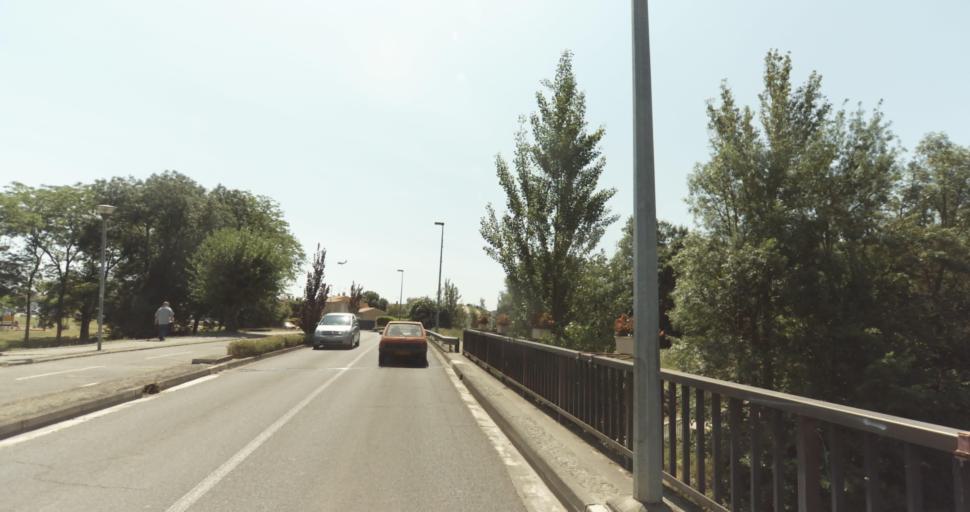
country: FR
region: Midi-Pyrenees
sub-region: Departement de la Haute-Garonne
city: Plaisance-du-Touch
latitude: 43.5632
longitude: 1.3001
